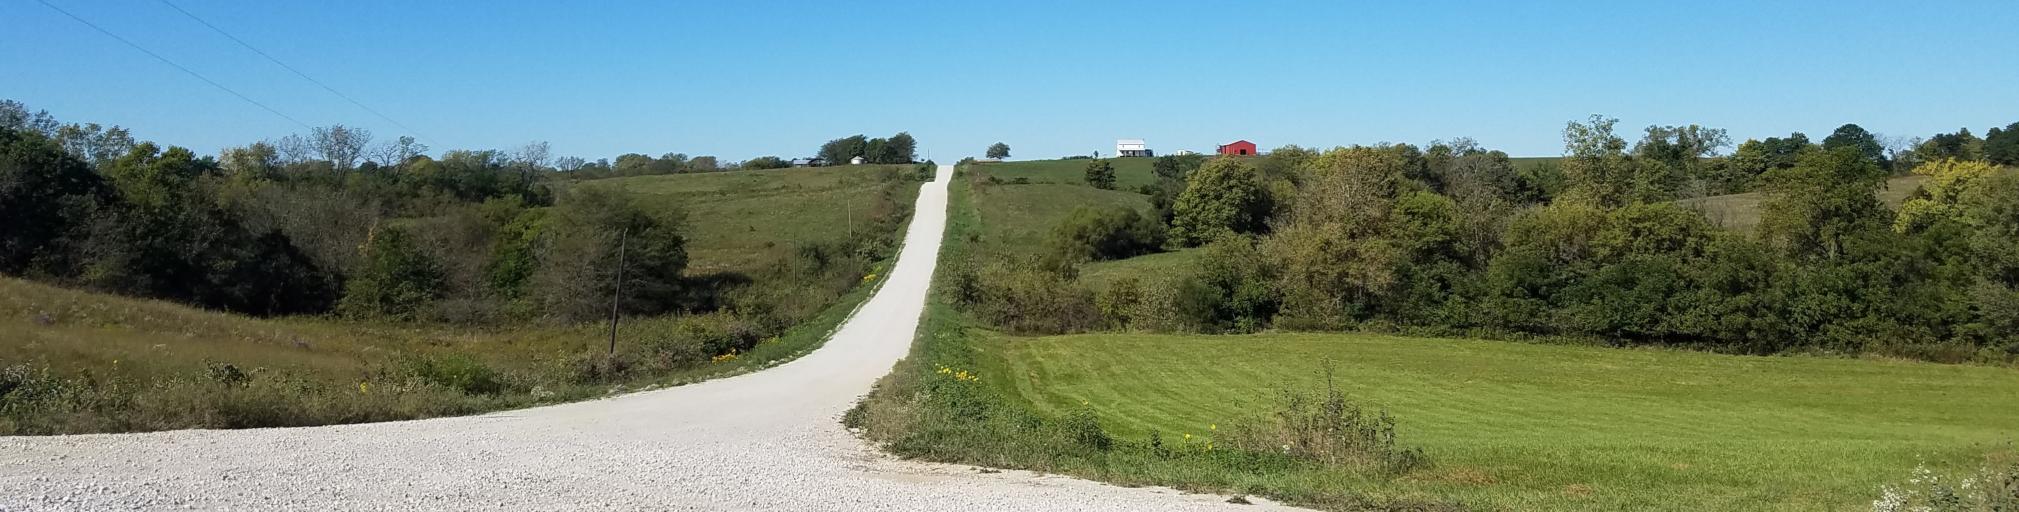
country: US
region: Iowa
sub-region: Decatur County
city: Lamoni
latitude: 40.6093
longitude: -93.8438
